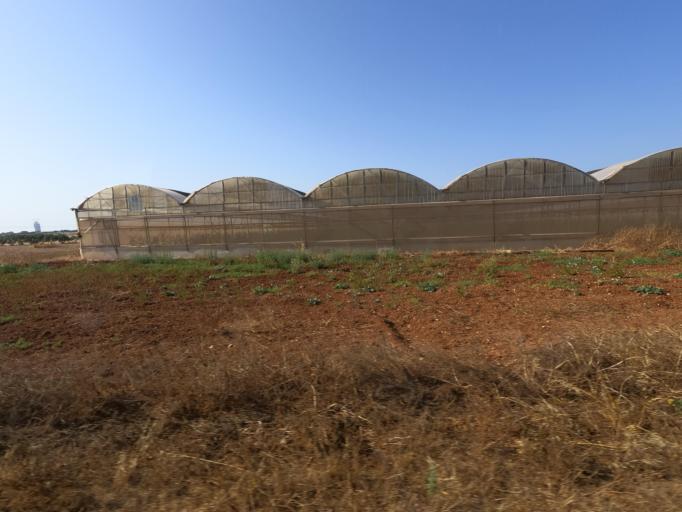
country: CY
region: Ammochostos
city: Liopetri
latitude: 34.9993
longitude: 33.9103
